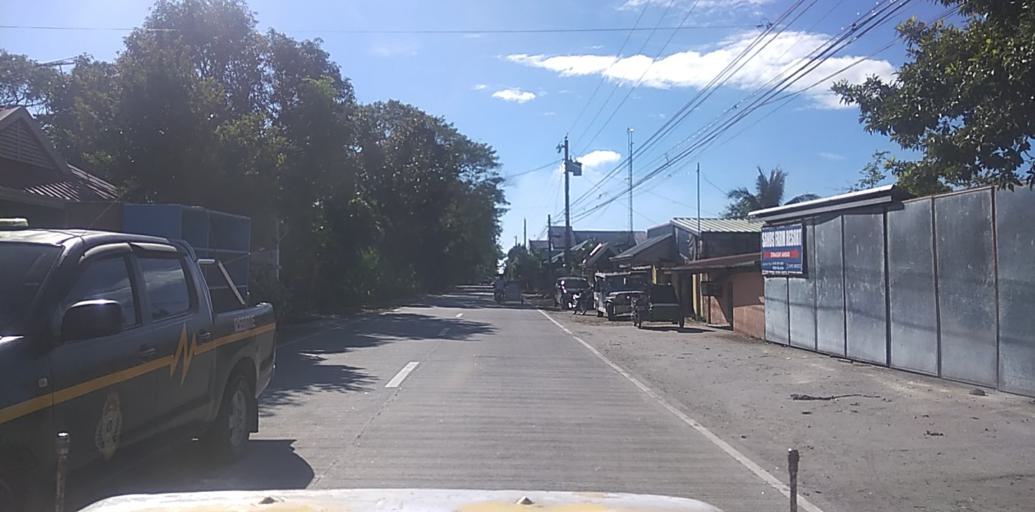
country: PH
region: Central Luzon
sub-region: Province of Pampanga
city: San Patricio
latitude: 15.0891
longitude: 120.7136
